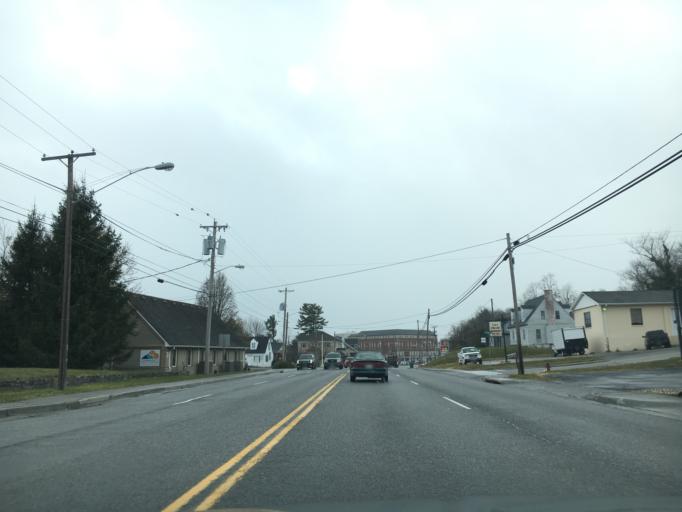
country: US
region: Virginia
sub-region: Montgomery County
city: Christiansburg
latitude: 37.1302
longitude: -80.4016
